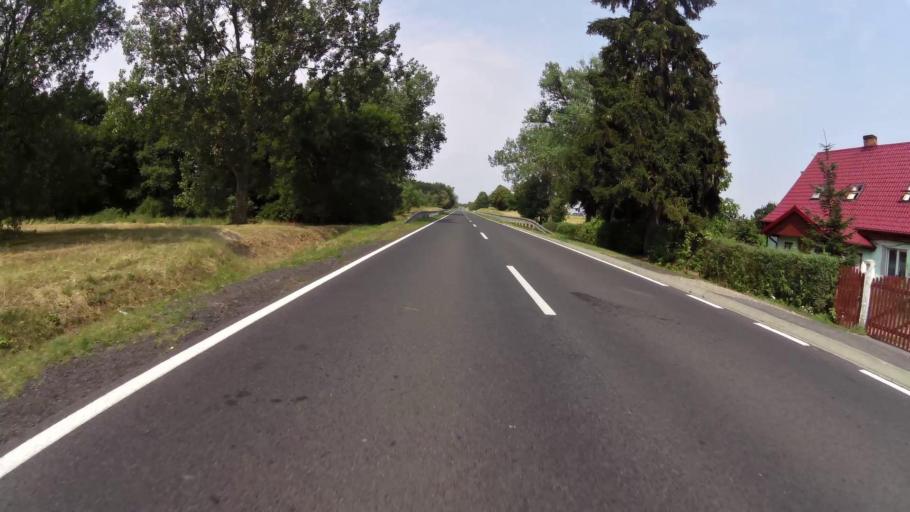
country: PL
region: West Pomeranian Voivodeship
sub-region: Powiat gryfinski
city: Mieszkowice
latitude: 52.8334
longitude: 14.4941
